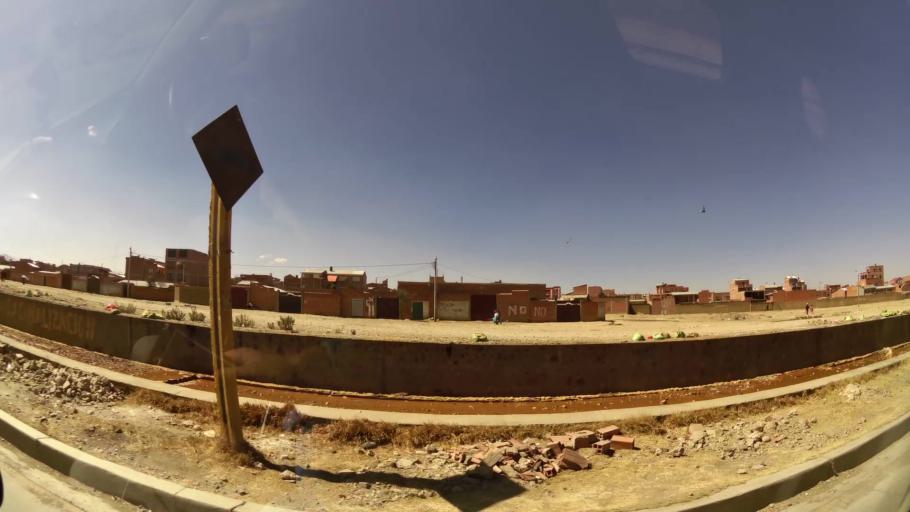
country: BO
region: La Paz
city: La Paz
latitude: -16.5020
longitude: -68.2094
